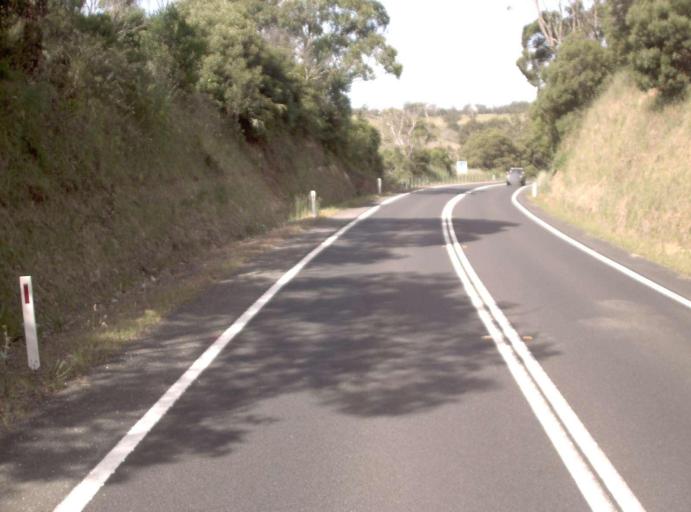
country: AU
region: Victoria
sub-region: East Gippsland
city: Lakes Entrance
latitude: -37.8540
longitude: 148.0325
